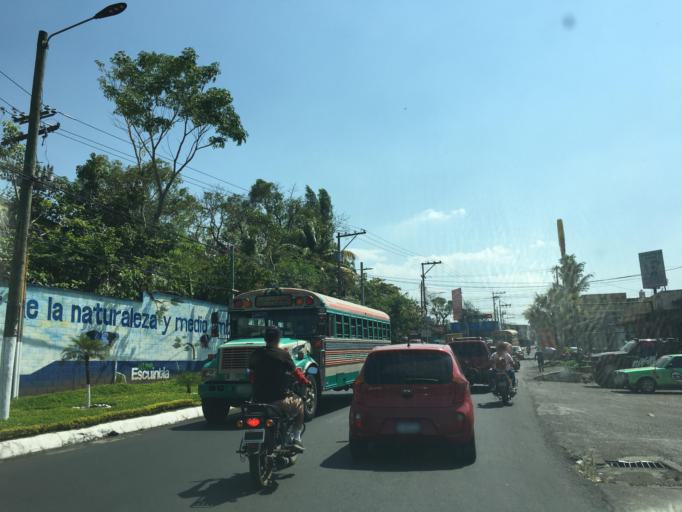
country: GT
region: Escuintla
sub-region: Municipio de Escuintla
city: Escuintla
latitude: 14.3055
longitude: -90.7889
